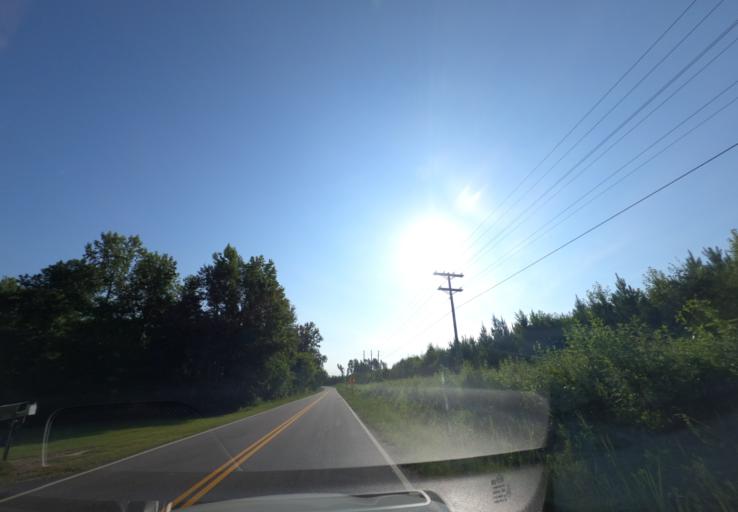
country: US
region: South Carolina
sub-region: Edgefield County
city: Murphys Estates
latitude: 33.5748
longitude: -81.9943
